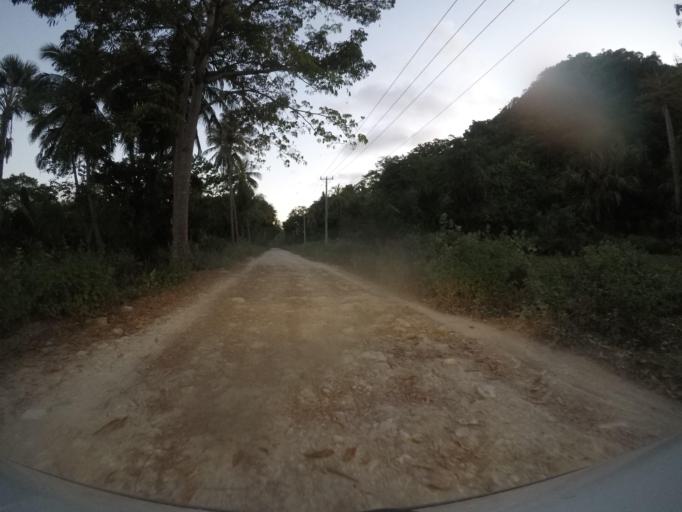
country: TL
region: Viqueque
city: Viqueque
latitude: -8.7927
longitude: 126.6247
